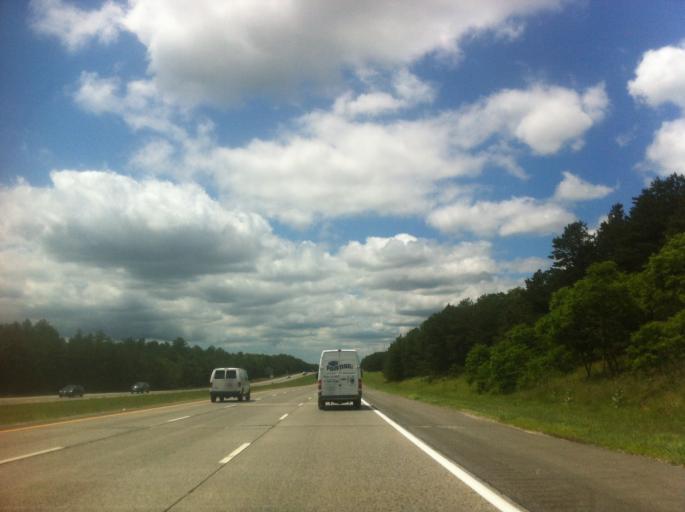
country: US
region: New York
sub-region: Suffolk County
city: Calverton
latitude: 40.8926
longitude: -72.7512
